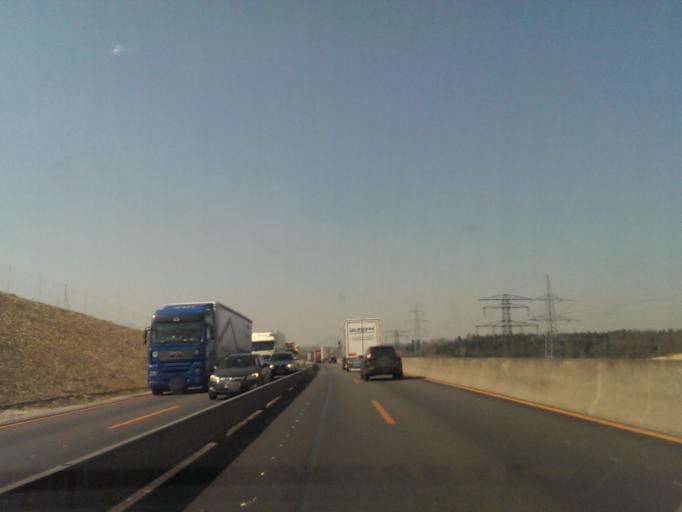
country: AT
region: Upper Austria
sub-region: Politischer Bezirk Vocklabruck
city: Wolfsegg am Hausruck
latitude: 48.1871
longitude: 13.6827
